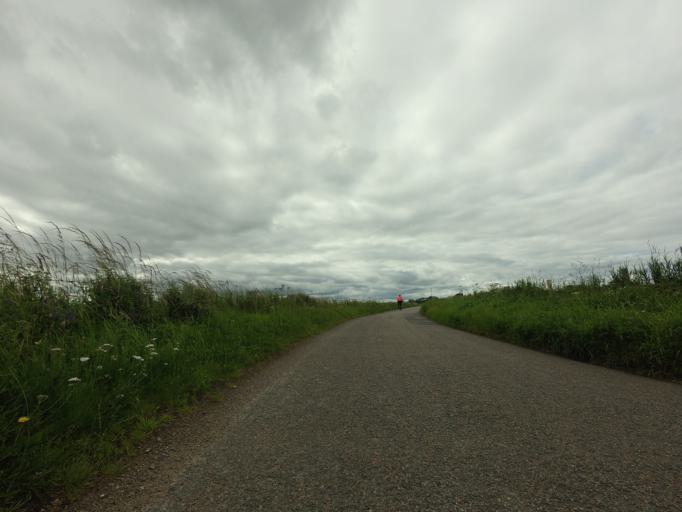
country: GB
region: Scotland
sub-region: Moray
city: Forres
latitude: 57.6274
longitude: -3.6034
